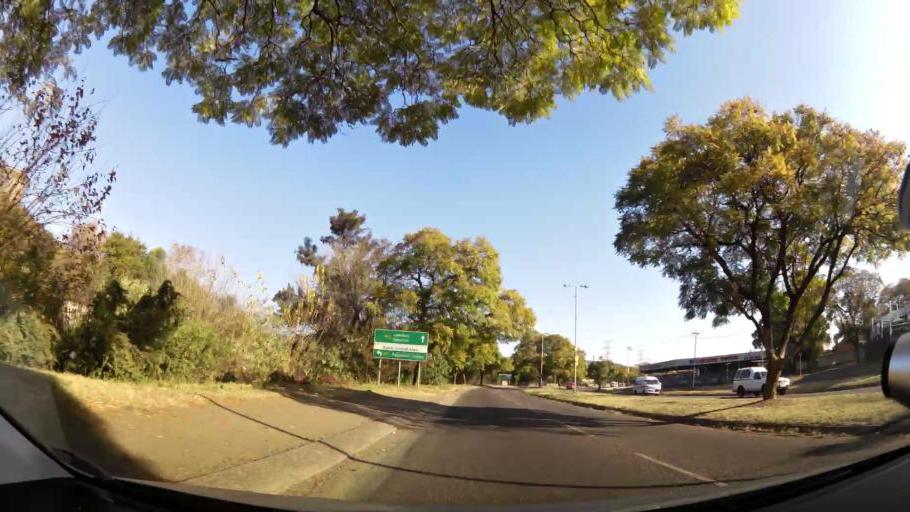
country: ZA
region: Gauteng
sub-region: City of Tshwane Metropolitan Municipality
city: Pretoria
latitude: -25.7571
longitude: 28.1422
